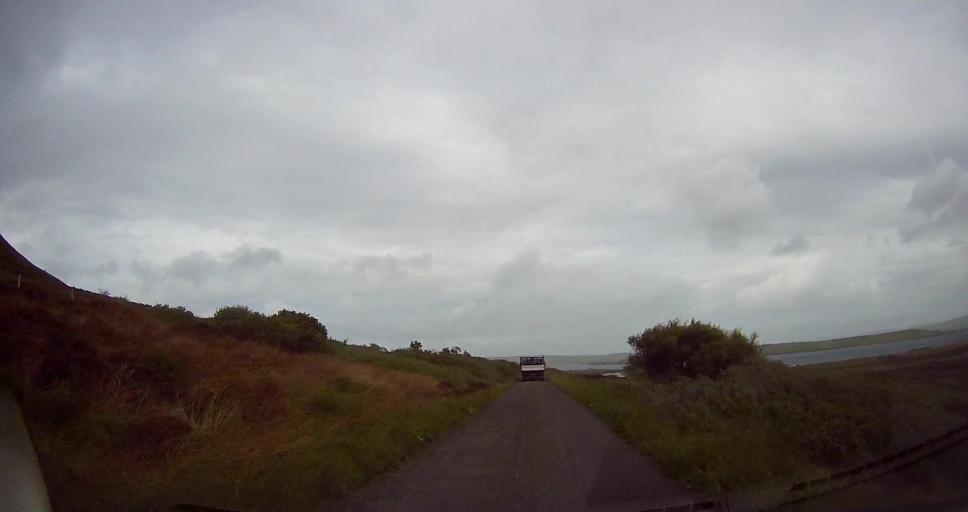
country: GB
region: Scotland
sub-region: Orkney Islands
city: Stromness
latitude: 58.8978
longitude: -3.3147
